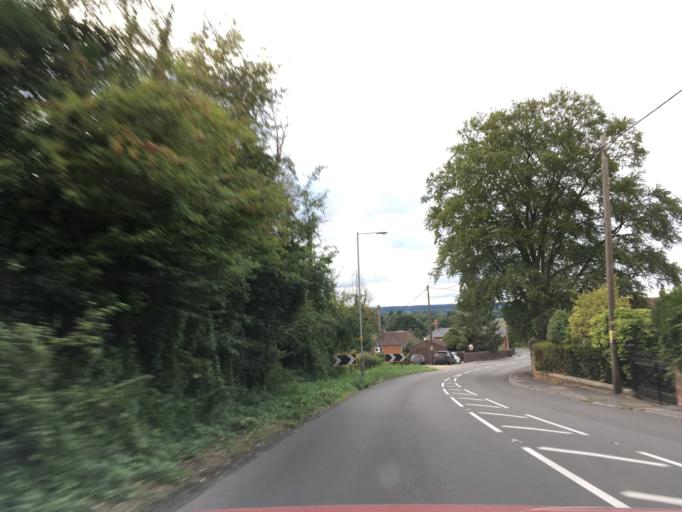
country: GB
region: England
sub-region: Wiltshire
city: Devizes
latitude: 51.3552
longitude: -2.0092
